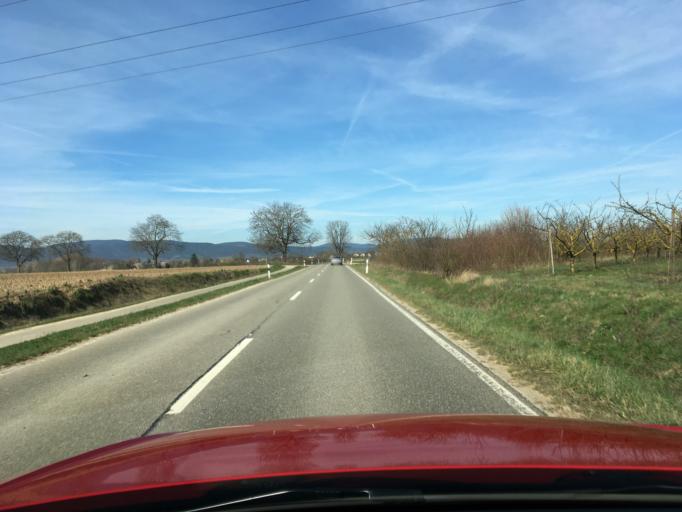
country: DE
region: Rheinland-Pfalz
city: Meckenheim
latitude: 49.3971
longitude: 8.2602
